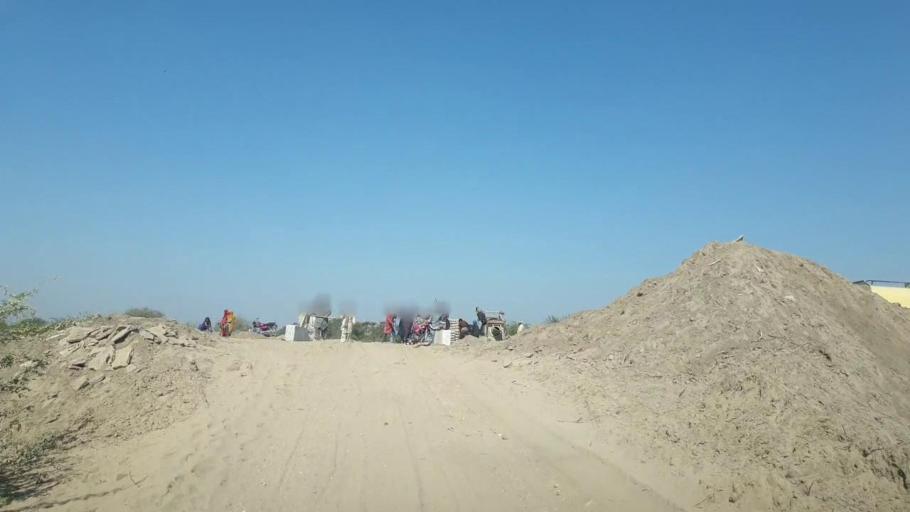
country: PK
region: Sindh
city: Mirpur Khas
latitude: 25.6479
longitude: 69.0273
